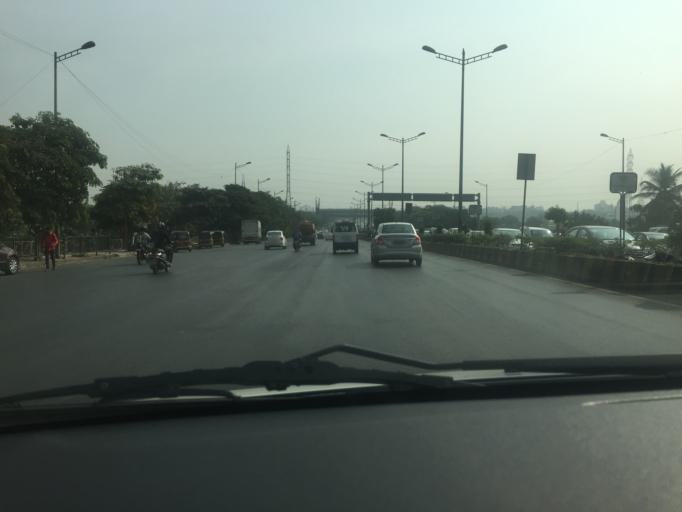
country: IN
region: Maharashtra
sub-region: Mumbai Suburban
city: Powai
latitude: 19.1250
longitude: 72.9286
